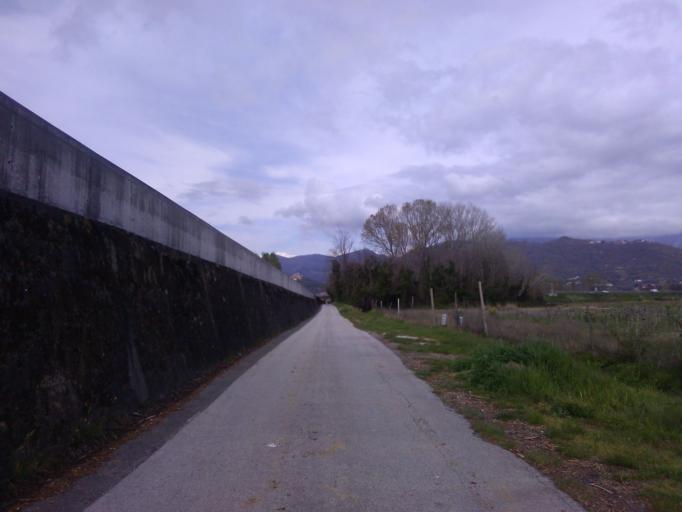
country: IT
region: Tuscany
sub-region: Provincia di Massa-Carrara
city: Marina di Carrara
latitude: 44.0520
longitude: 10.0238
